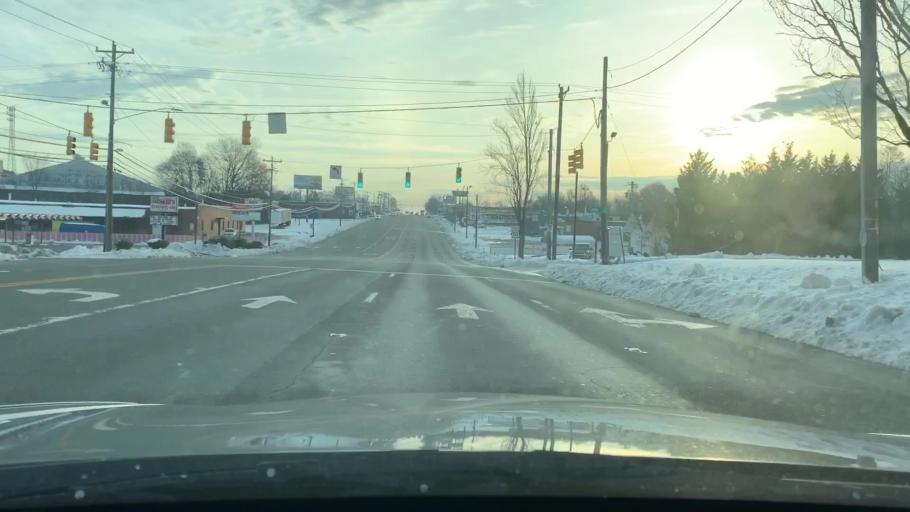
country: US
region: North Carolina
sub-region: Alamance County
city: Burlington
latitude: 36.0964
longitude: -79.4115
